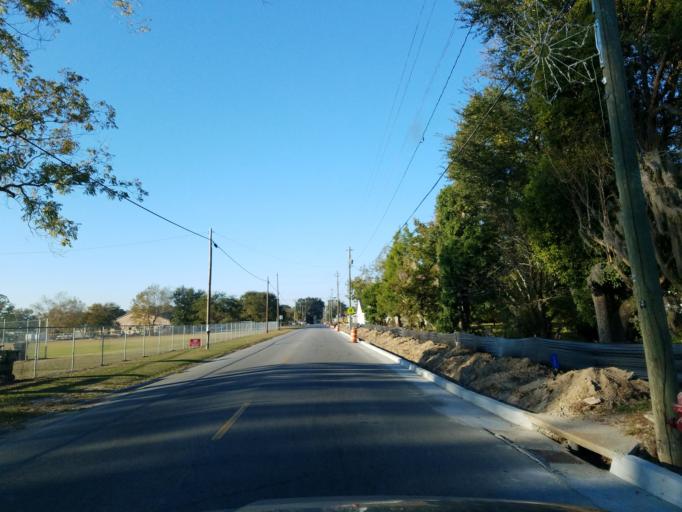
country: US
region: Georgia
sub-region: Lanier County
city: Lakeland
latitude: 31.0327
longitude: -83.0685
